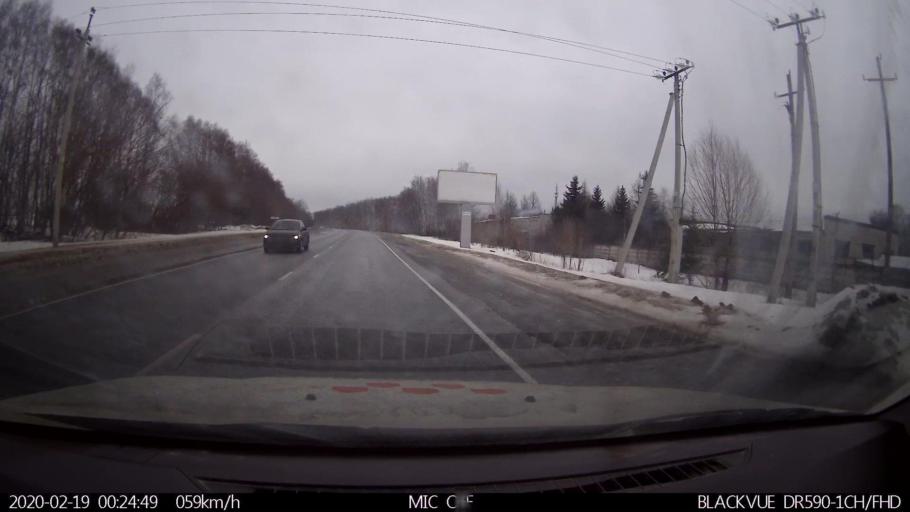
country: RU
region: Nizjnij Novgorod
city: Nizhniy Novgorod
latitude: 56.2196
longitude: 43.9401
